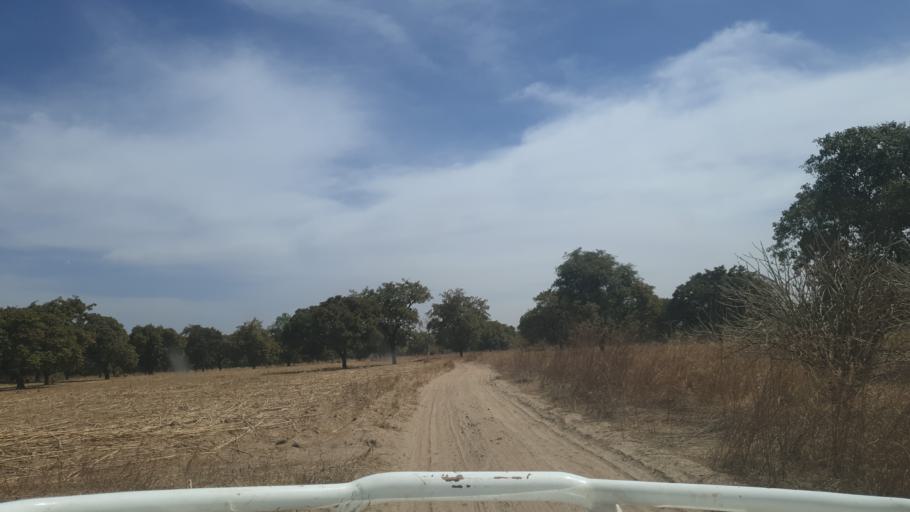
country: ML
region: Sikasso
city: Yorosso
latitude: 12.2870
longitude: -4.6778
